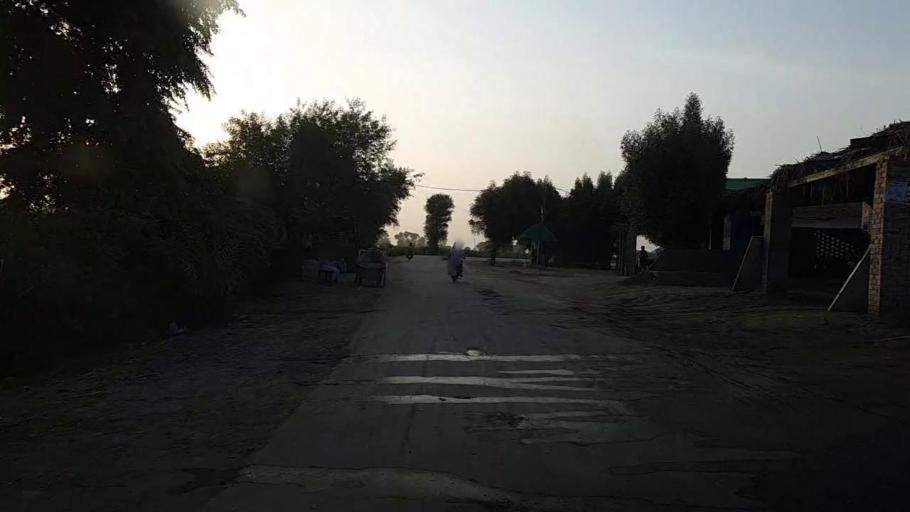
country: PK
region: Sindh
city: Ubauro
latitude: 28.2202
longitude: 69.8204
